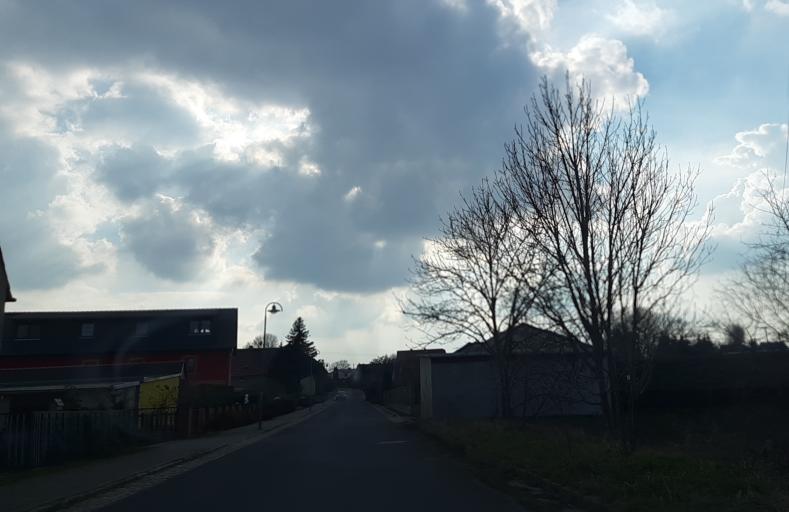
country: DE
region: Saxony
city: Wildenhain
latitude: 51.2888
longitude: 13.4745
